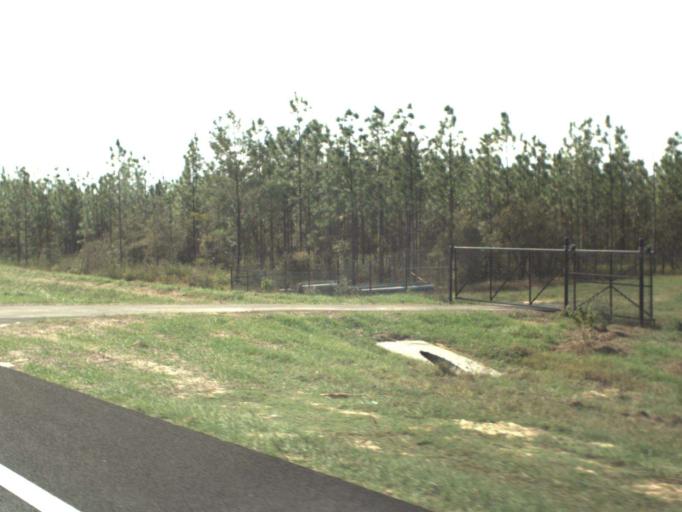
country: US
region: Florida
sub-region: Holmes County
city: Bonifay
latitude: 30.5602
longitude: -85.8138
